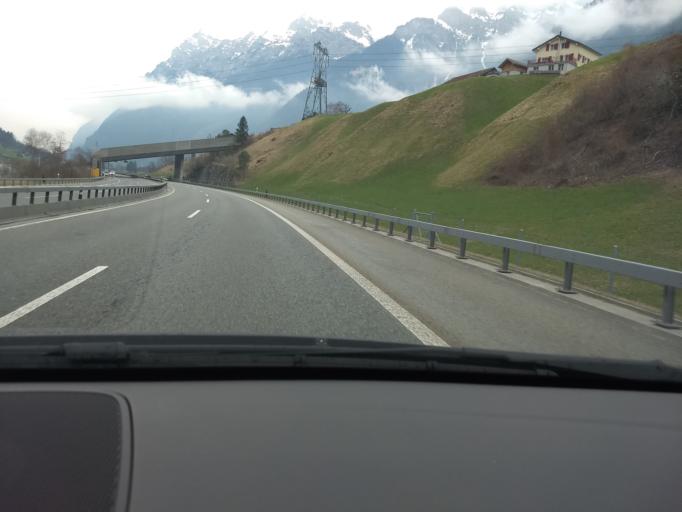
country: CH
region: Uri
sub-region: Uri
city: Silenen
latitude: 46.7822
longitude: 8.6691
